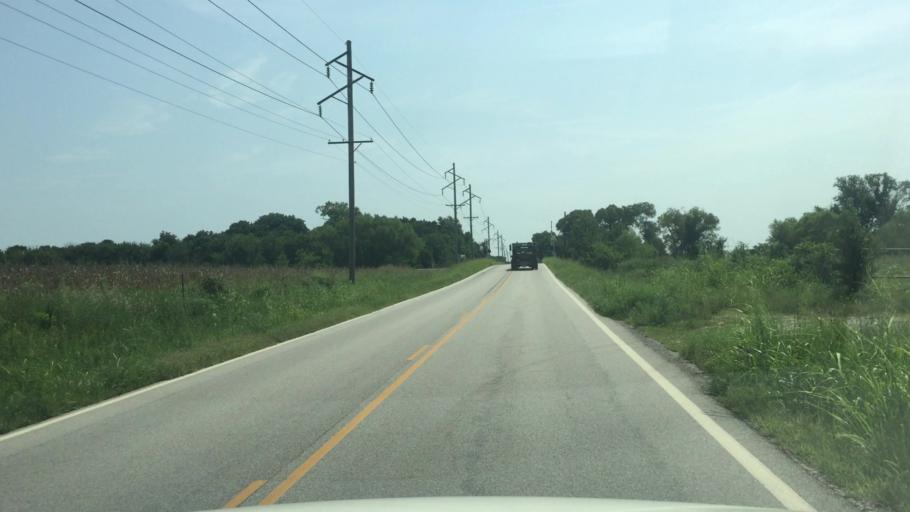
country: US
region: Kansas
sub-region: Montgomery County
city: Cherryvale
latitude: 37.2082
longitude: -95.5672
